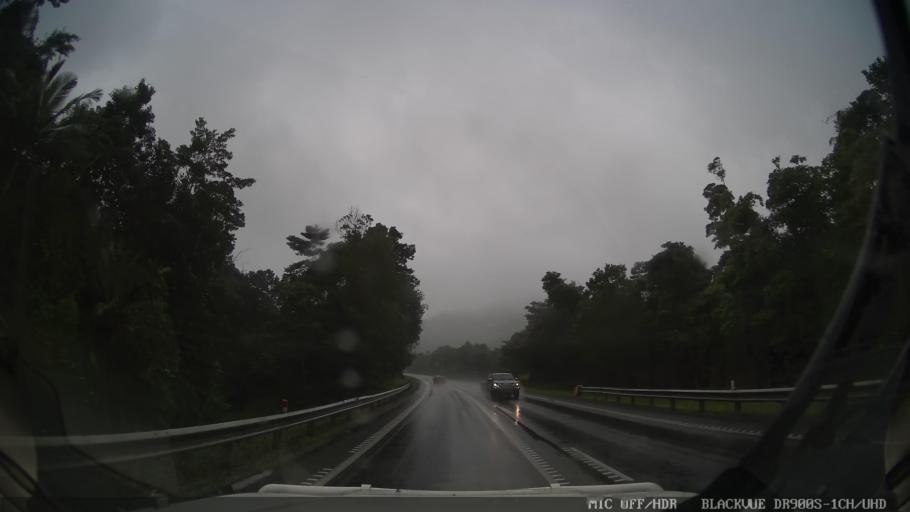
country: AU
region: Queensland
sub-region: Cassowary Coast
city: Innisfail
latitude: -17.8639
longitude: 145.9840
